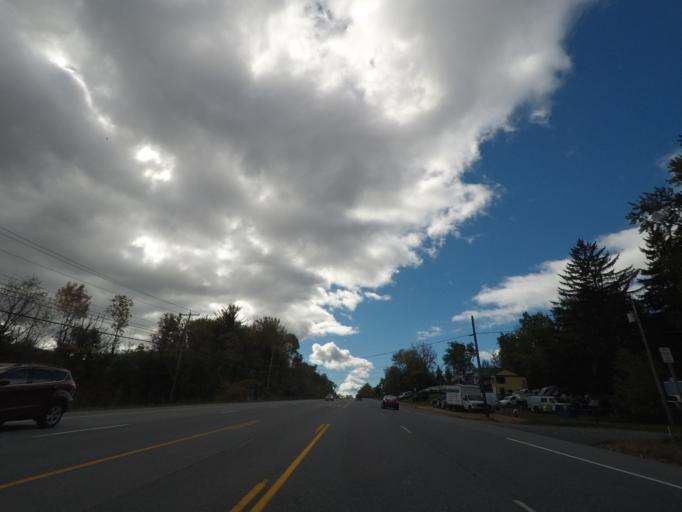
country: US
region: New York
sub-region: Albany County
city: Cohoes
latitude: 42.8119
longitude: -73.7320
